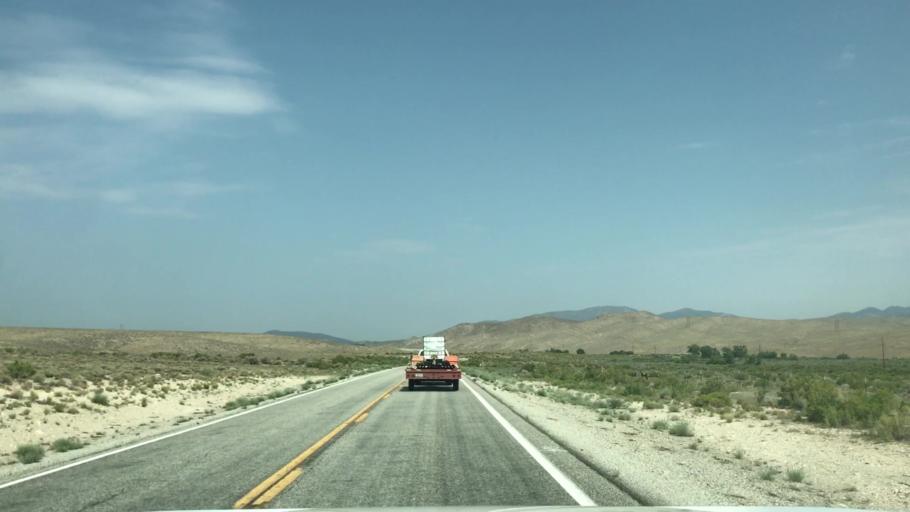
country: US
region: Nevada
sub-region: White Pine County
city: McGill
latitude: 39.0799
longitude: -114.1915
